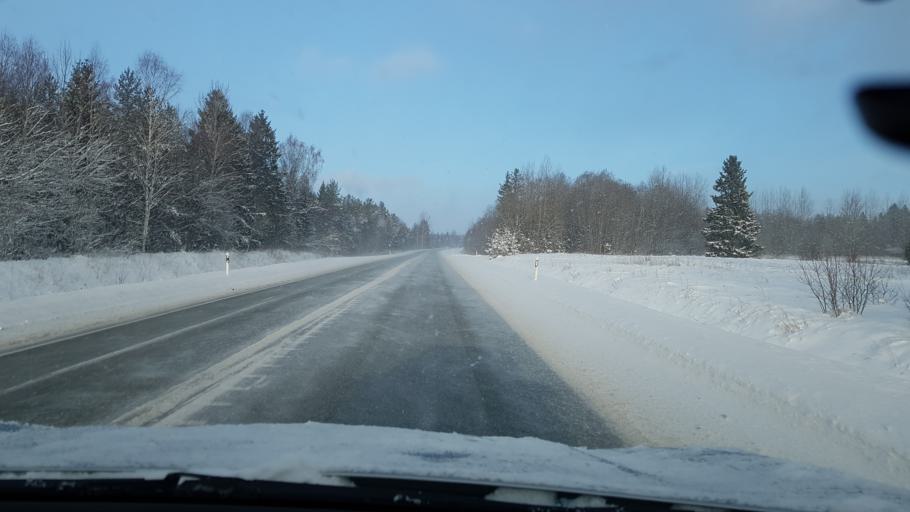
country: EE
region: Harju
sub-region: Nissi vald
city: Riisipere
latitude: 59.1551
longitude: 24.3405
